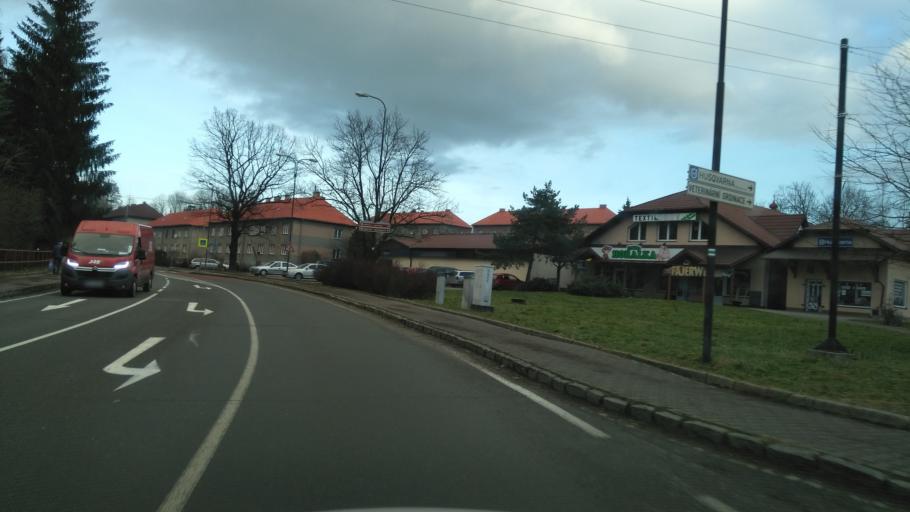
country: CZ
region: Moravskoslezsky
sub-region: Okres Frydek-Mistek
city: Jablunkov
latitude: 49.5786
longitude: 18.7668
